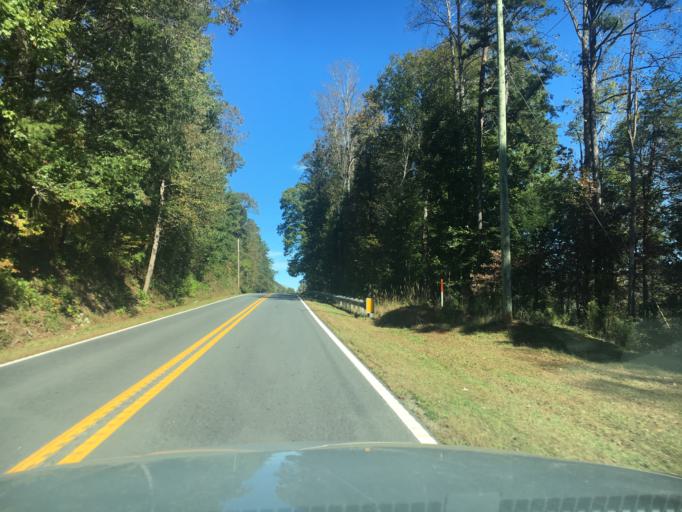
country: US
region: North Carolina
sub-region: Rutherford County
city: Spindale
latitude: 35.5081
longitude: -81.8562
